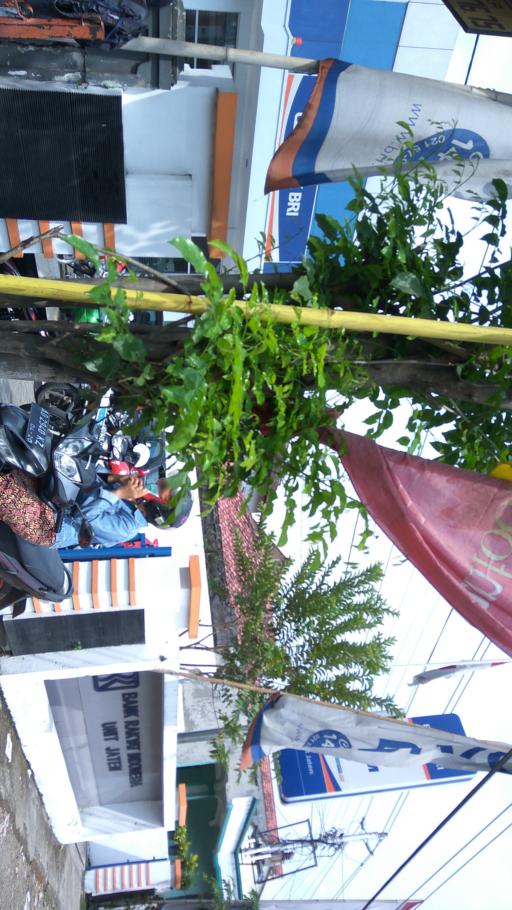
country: ID
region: Central Java
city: Jaten
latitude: -7.5745
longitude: 110.8863
